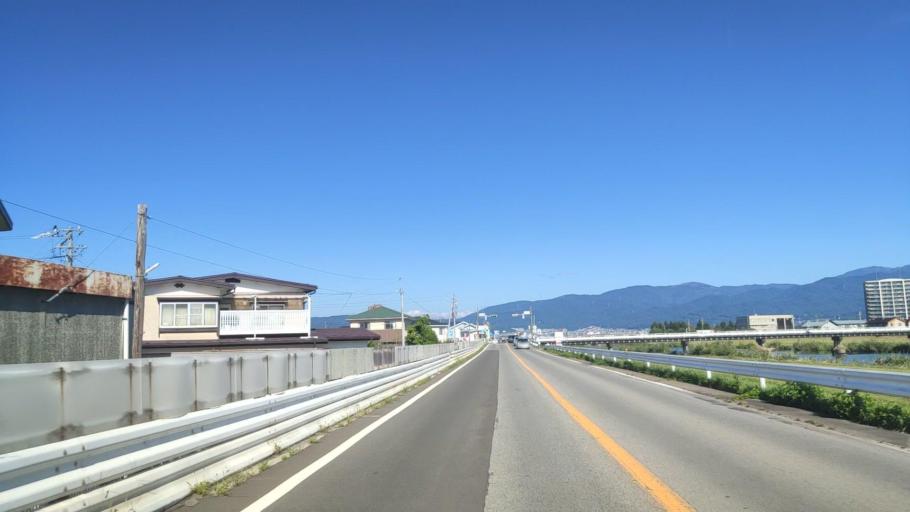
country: JP
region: Nagano
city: Suwa
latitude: 36.0340
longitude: 138.1048
